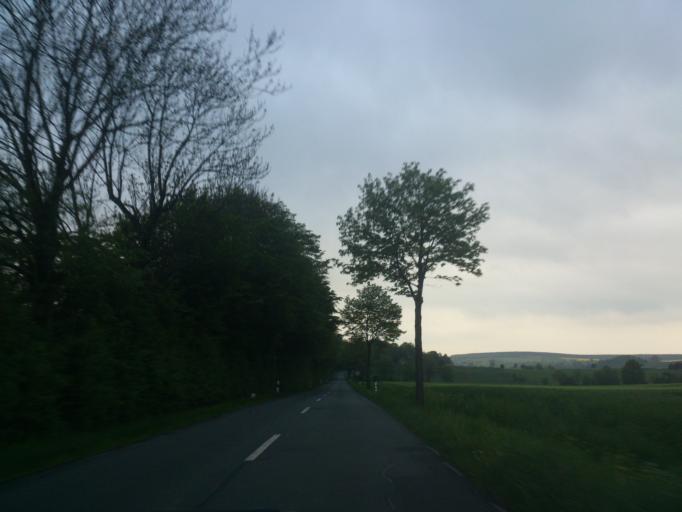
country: DE
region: North Rhine-Westphalia
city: Lichtenau
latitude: 51.6719
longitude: 8.9411
